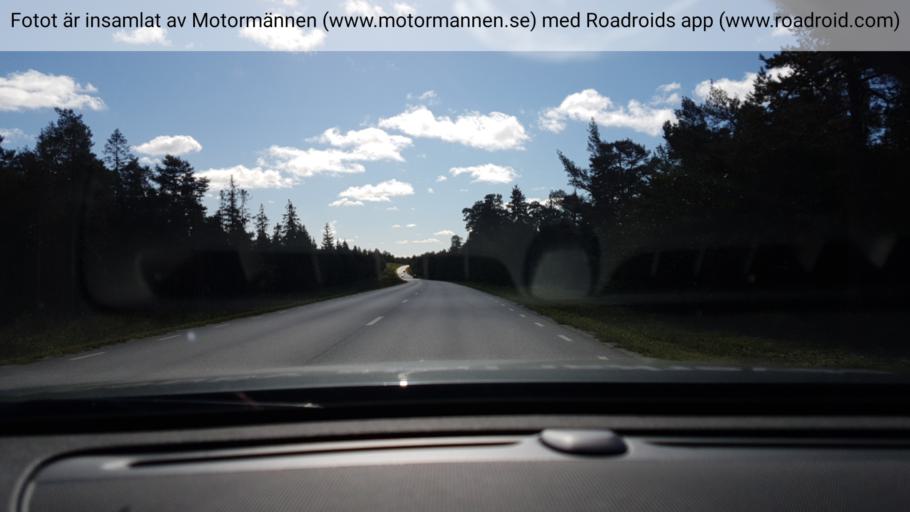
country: SE
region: Gotland
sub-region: Gotland
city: Slite
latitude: 57.7453
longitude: 18.7893
